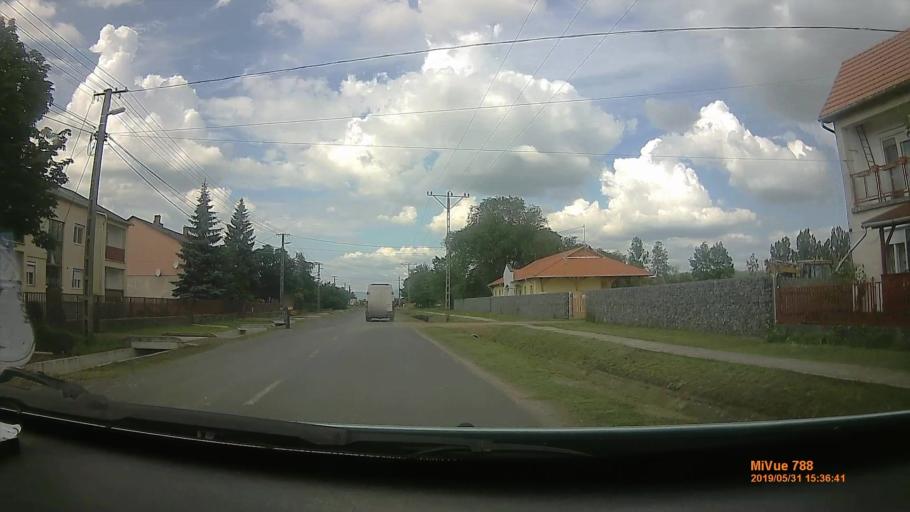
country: HU
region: Borsod-Abauj-Zemplen
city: Prugy
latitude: 48.0858
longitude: 21.2404
